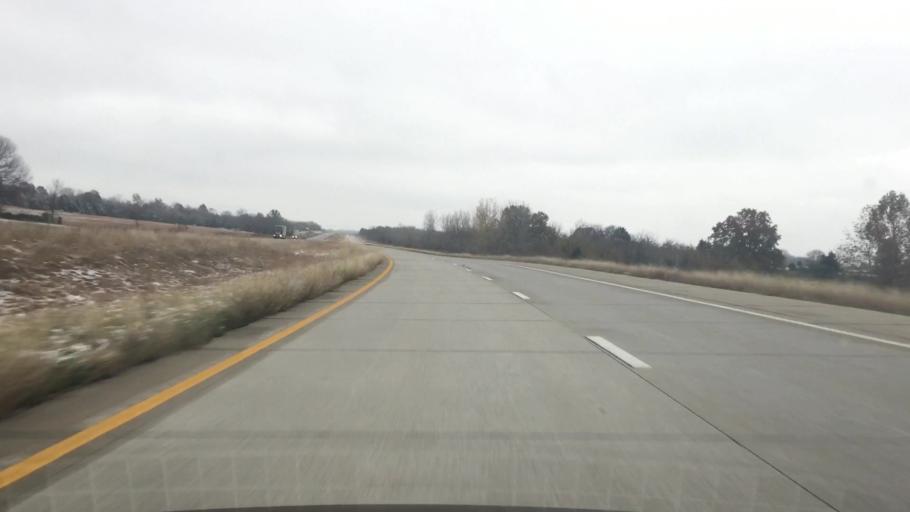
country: US
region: Missouri
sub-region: Henry County
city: Clinton
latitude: 38.2142
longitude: -93.7598
